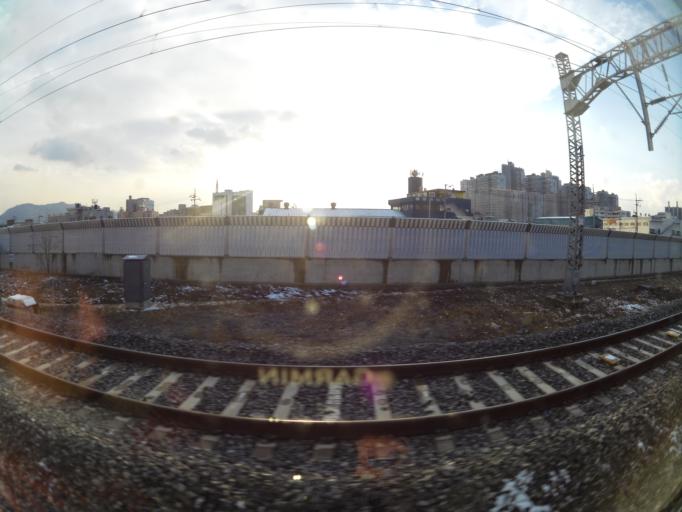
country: KR
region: Daejeon
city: Daejeon
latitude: 36.3405
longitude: 127.4299
